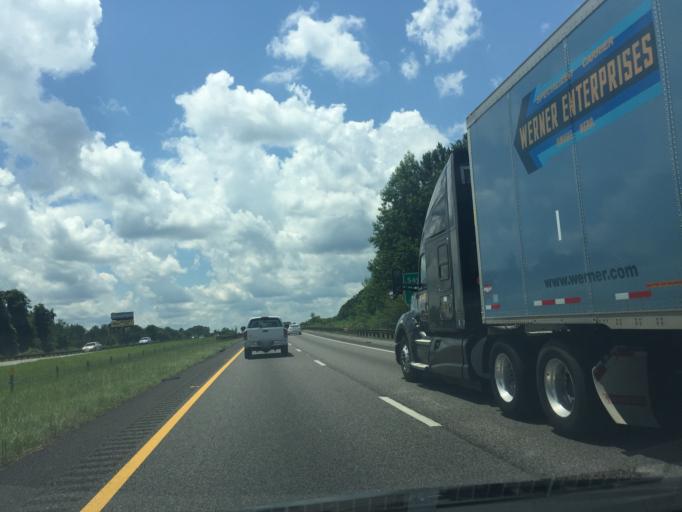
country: US
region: South Carolina
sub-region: Jasper County
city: Hardeeville
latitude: 32.2538
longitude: -81.1118
